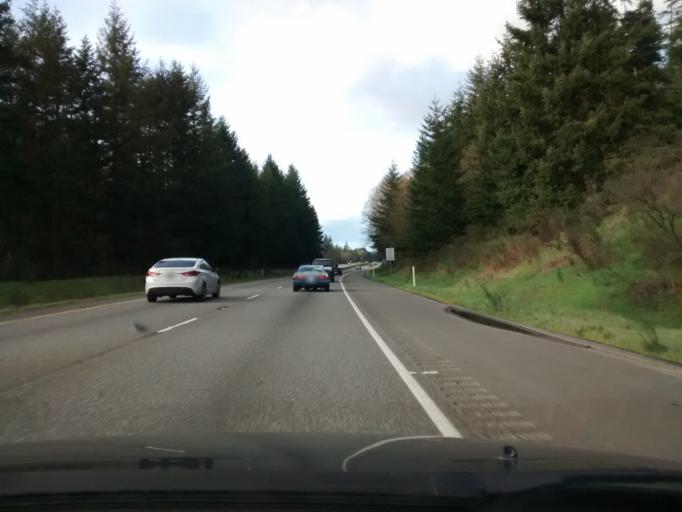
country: US
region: Washington
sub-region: Kitsap County
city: Burley
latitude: 47.4238
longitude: -122.6234
